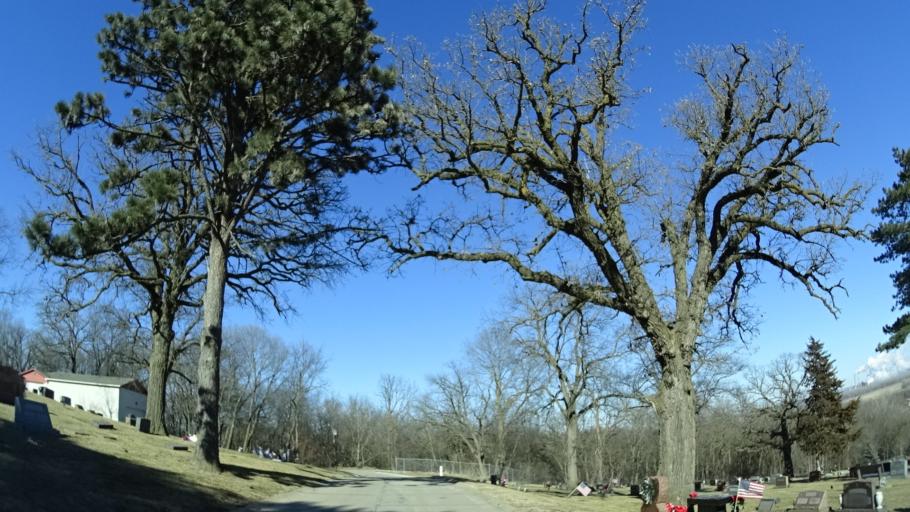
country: US
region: Nebraska
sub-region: Sarpy County
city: Bellevue
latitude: 41.1496
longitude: -95.8946
